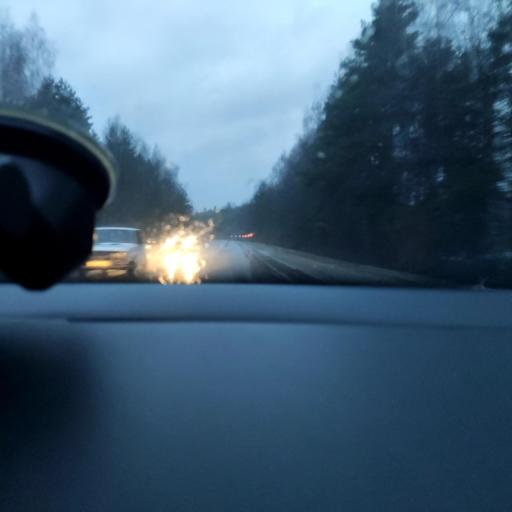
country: RU
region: Moskovskaya
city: Krasnyy Tkach
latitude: 55.4032
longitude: 39.1404
